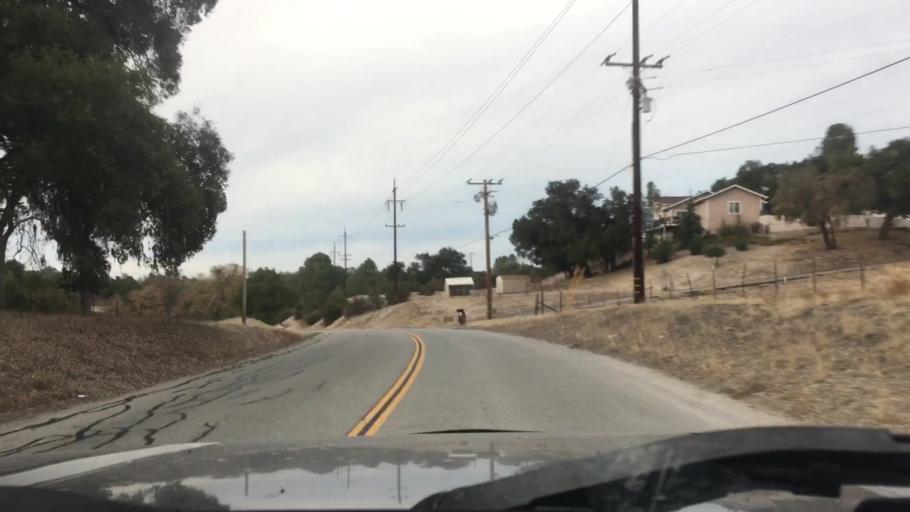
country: US
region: California
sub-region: San Luis Obispo County
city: Atascadero
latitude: 35.4442
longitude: -120.6457
